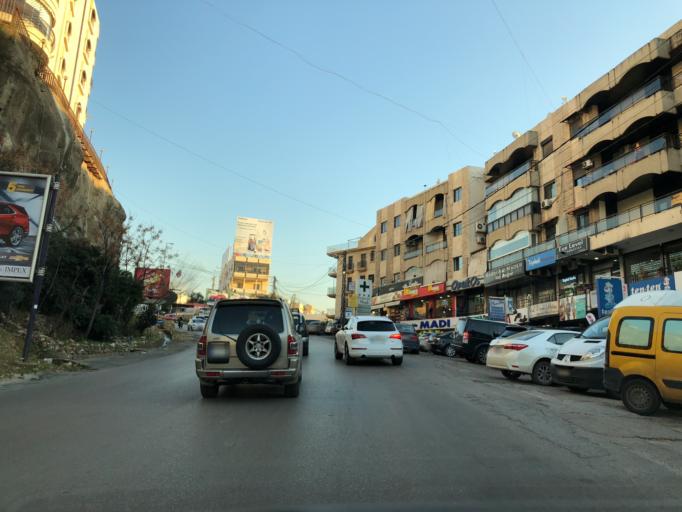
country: LB
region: Mont-Liban
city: Baabda
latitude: 33.8545
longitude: 35.5639
